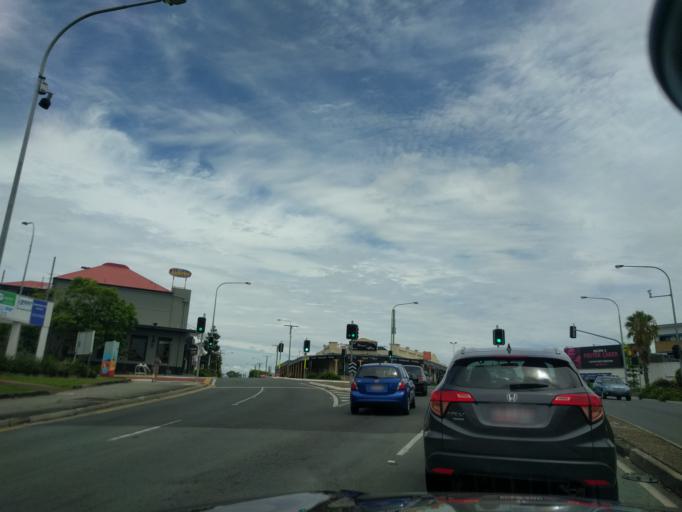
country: AU
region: Queensland
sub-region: Brisbane
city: Grange
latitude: -27.4256
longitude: 153.0014
